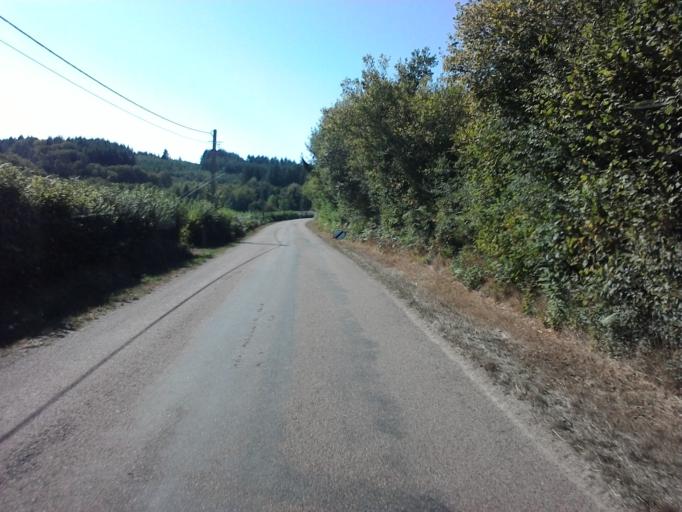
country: FR
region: Bourgogne
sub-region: Departement de la Nievre
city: Lormes
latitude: 47.2833
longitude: 3.9985
